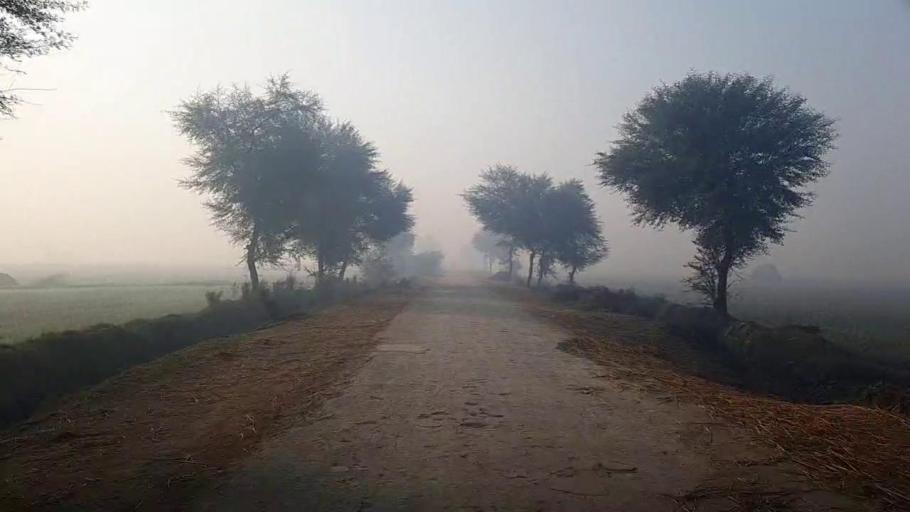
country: PK
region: Sindh
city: Mehar
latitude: 27.1609
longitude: 67.8242
